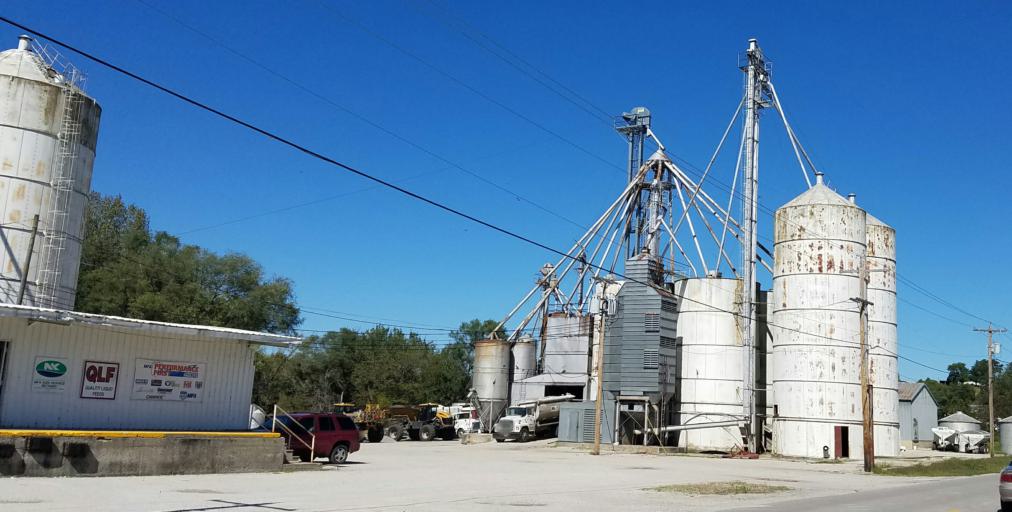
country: US
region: Missouri
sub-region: Harrison County
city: Bethany
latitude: 40.2776
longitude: -94.0267
